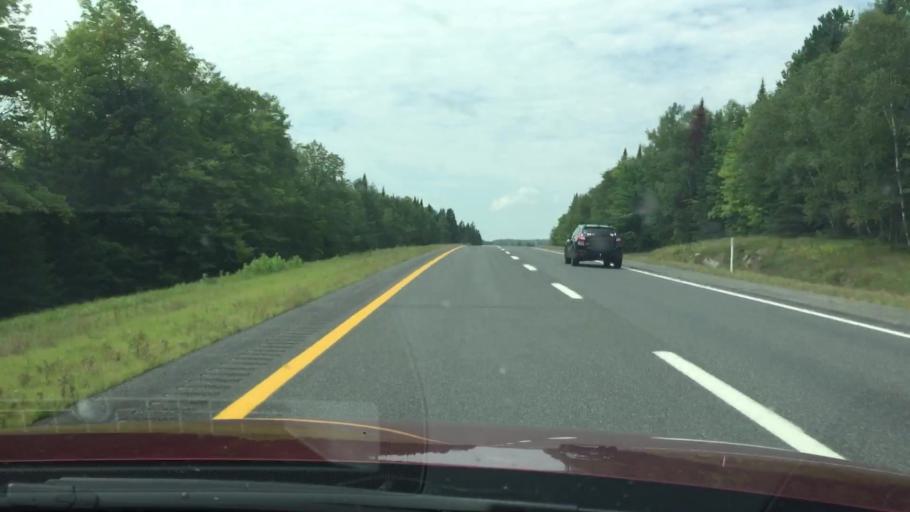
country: US
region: Maine
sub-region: Aroostook County
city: Hodgdon
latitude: 46.1407
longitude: -68.0185
